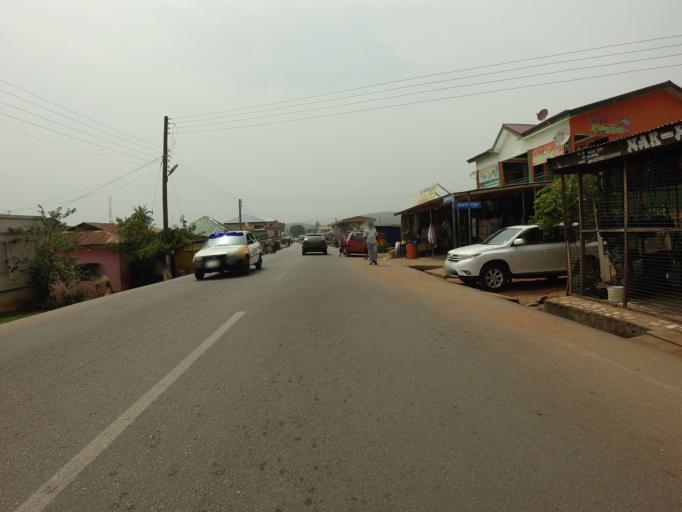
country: GH
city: Akropong
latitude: 6.1013
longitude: -0.0165
